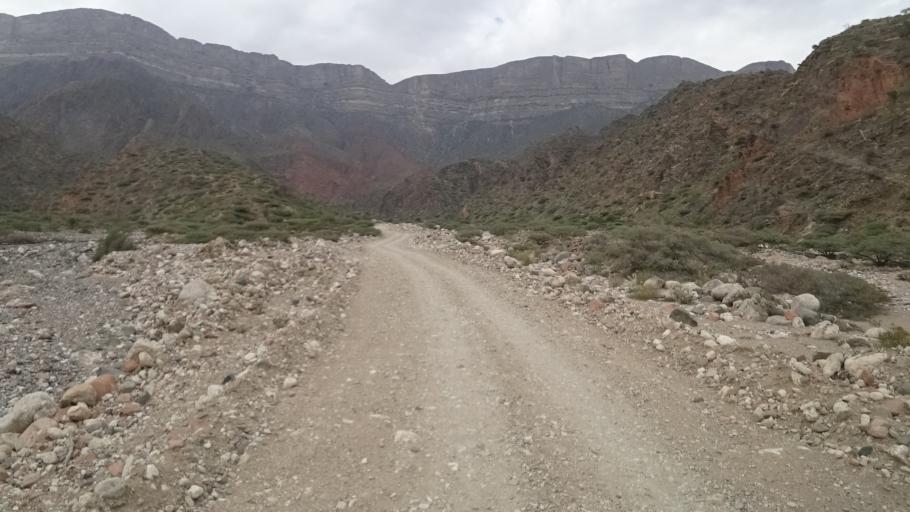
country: OM
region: Zufar
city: Salalah
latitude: 17.1793
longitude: 54.9479
